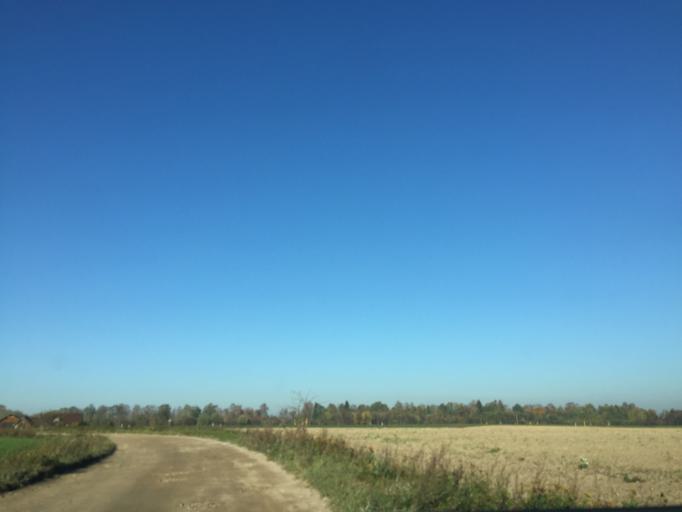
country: LT
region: Klaipedos apskritis
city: Kretinga
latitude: 55.8518
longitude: 21.2139
